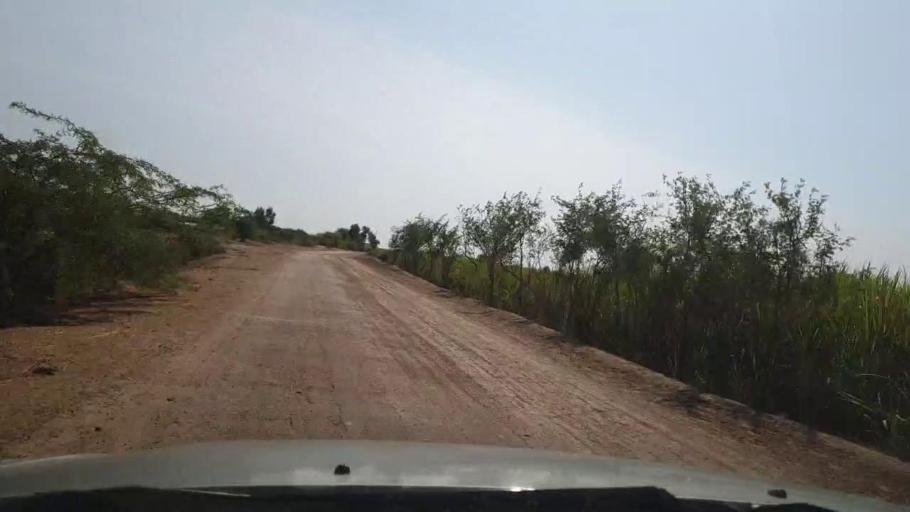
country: PK
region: Sindh
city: Bulri
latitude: 25.0039
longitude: 68.3200
